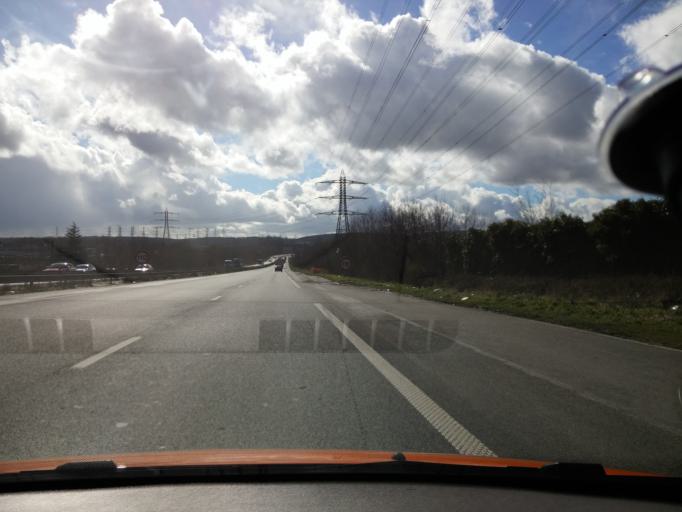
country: FR
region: Ile-de-France
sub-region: Departement de l'Essonne
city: Palaiseau
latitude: 48.7133
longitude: 2.2527
